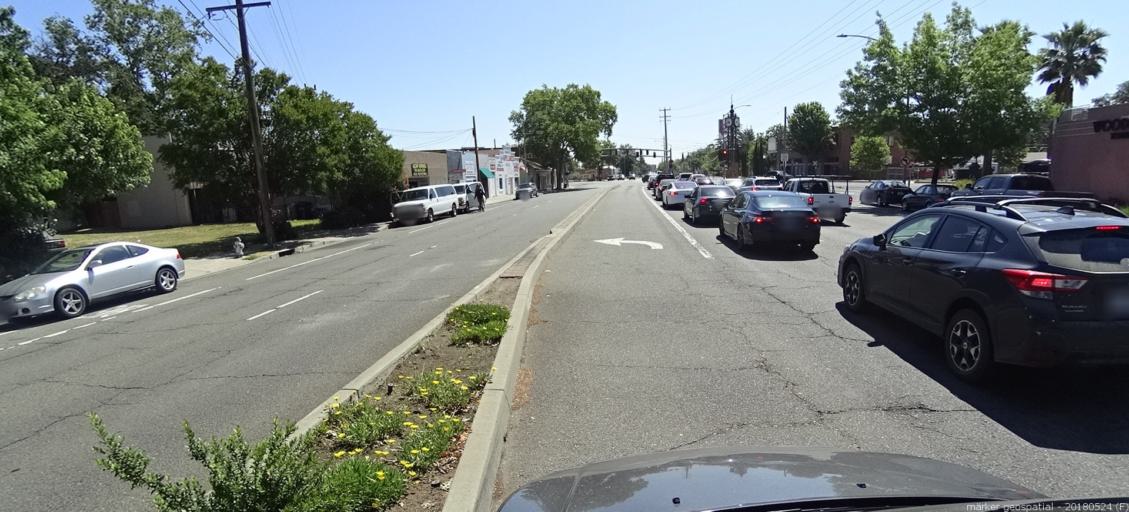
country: US
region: California
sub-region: Sacramento County
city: Sacramento
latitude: 38.6063
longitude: -121.4600
